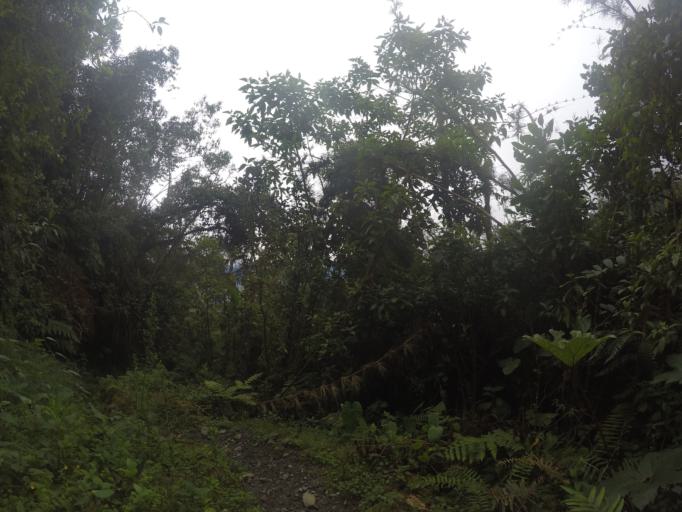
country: CO
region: Tolima
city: Cajamarca
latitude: 4.5377
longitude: -75.3440
